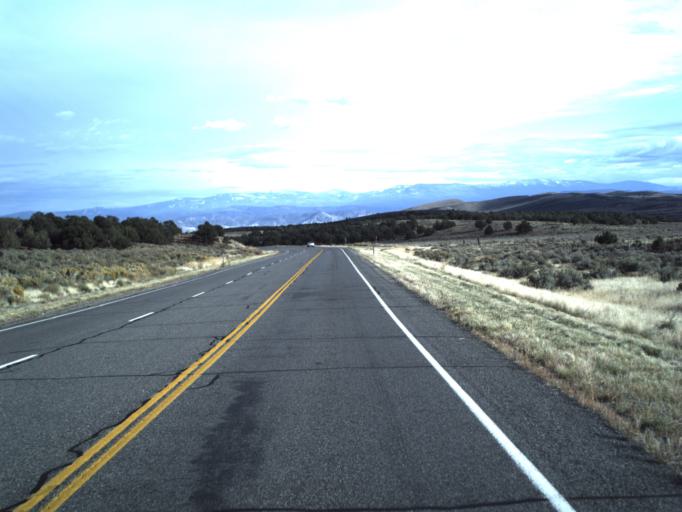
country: US
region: Utah
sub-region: Sevier County
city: Aurora
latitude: 38.9998
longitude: -112.0228
